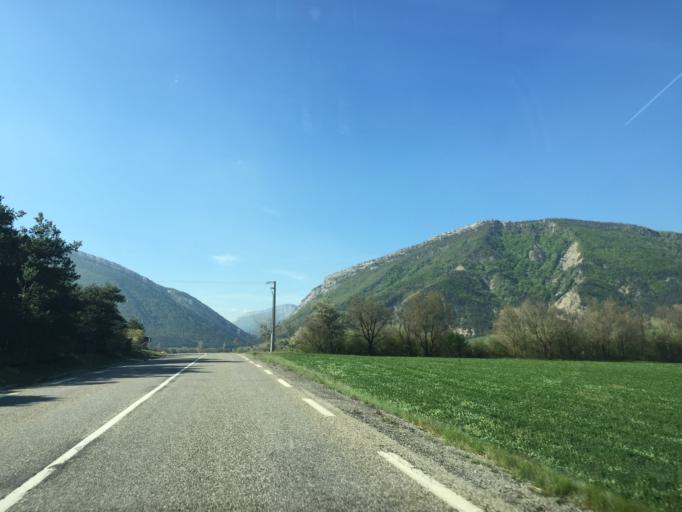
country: FR
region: Provence-Alpes-Cote d'Azur
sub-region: Departement des Hautes-Alpes
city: Serres
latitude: 44.4689
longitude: 5.7251
